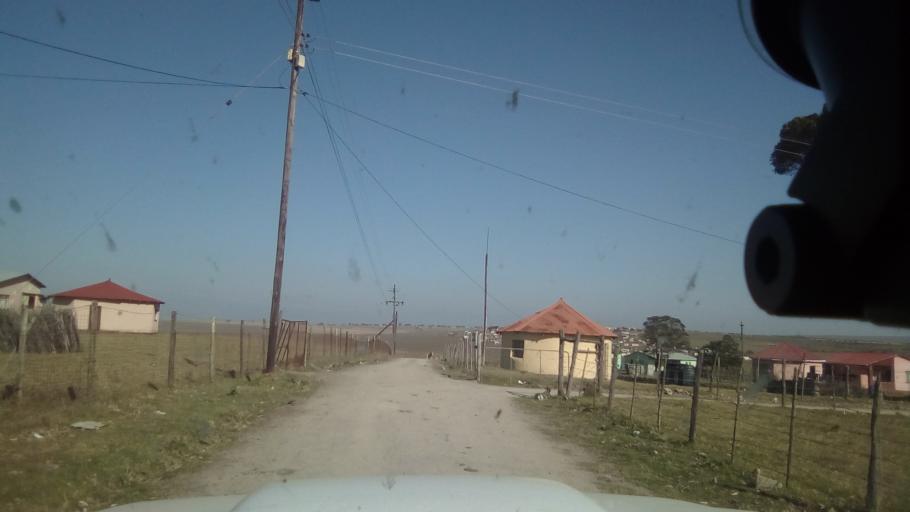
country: ZA
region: Eastern Cape
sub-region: Buffalo City Metropolitan Municipality
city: Bhisho
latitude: -32.9415
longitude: 27.3322
